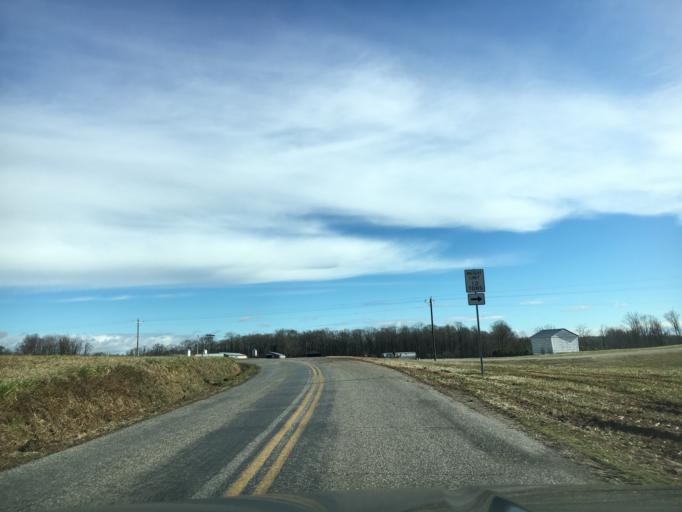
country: US
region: Virginia
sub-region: Amelia County
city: Amelia Court House
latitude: 37.3809
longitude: -78.1291
